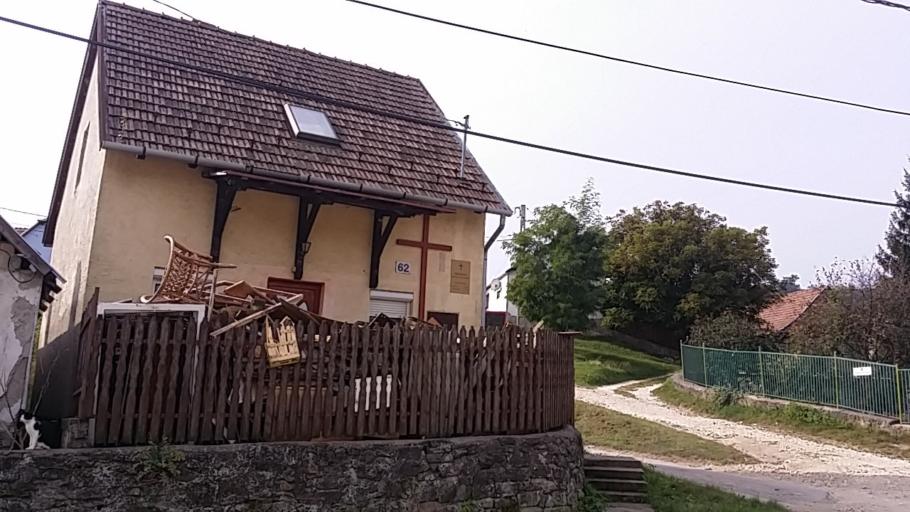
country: HU
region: Pest
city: Csobanka
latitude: 47.6466
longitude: 18.9588
